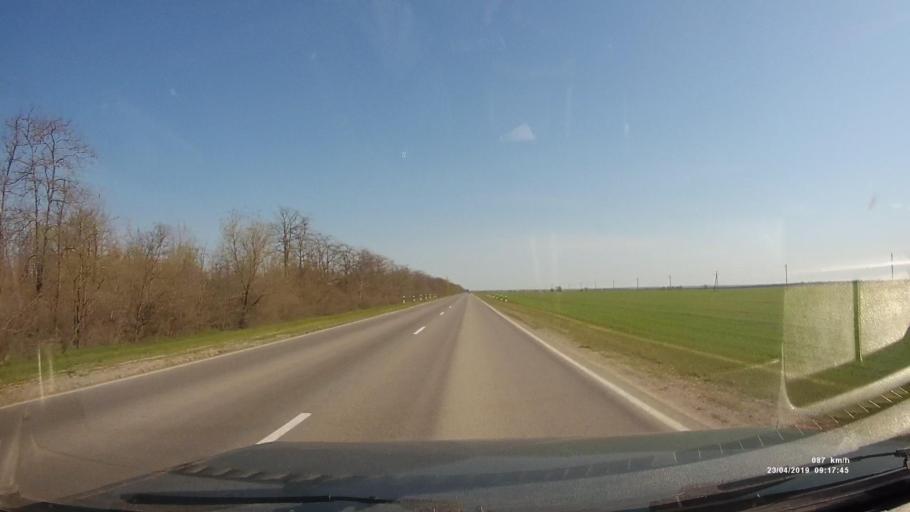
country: RU
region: Rostov
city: Proletarsk
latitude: 46.6550
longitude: 41.6809
